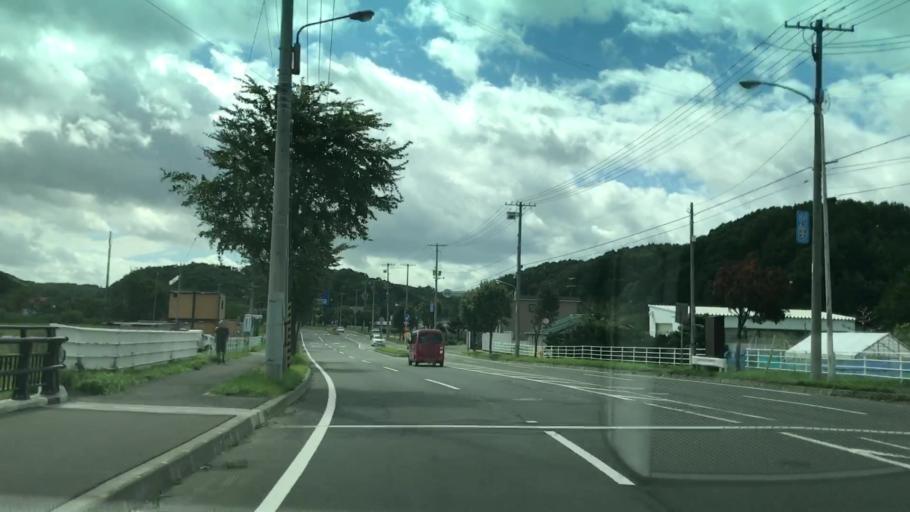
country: JP
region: Hokkaido
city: Sapporo
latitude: 42.9826
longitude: 141.4380
